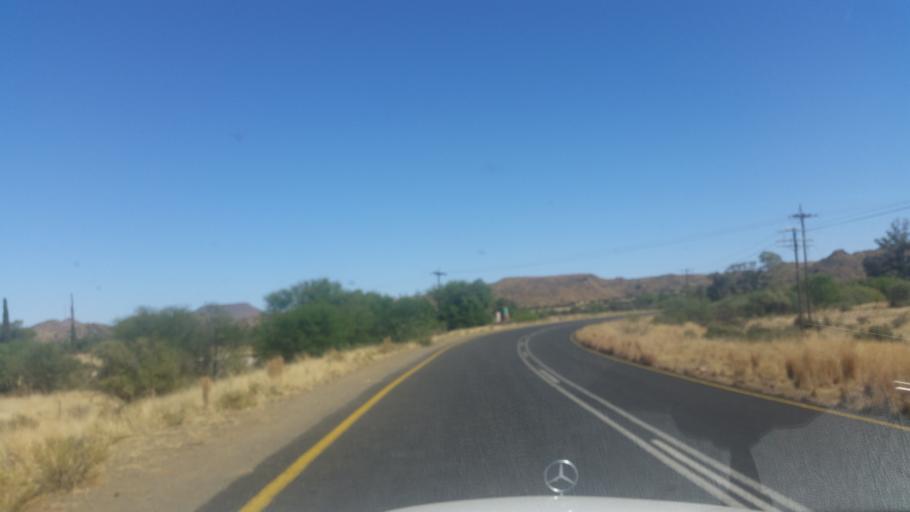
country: ZA
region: Orange Free State
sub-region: Xhariep District Municipality
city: Trompsburg
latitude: -30.4928
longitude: 25.9947
